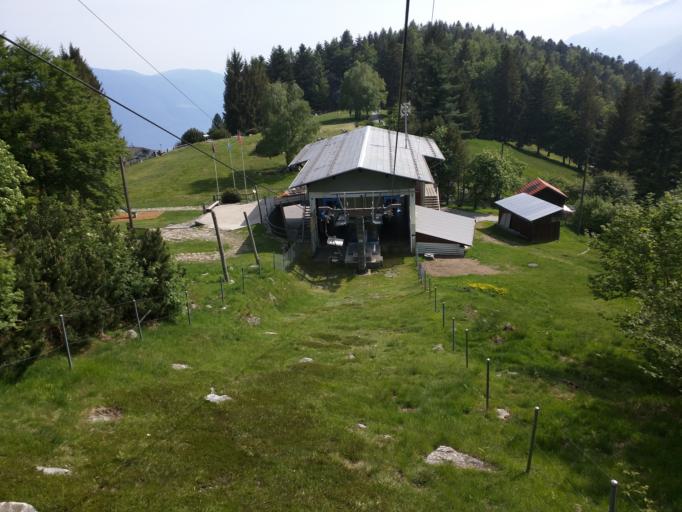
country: CH
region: Ticino
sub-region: Locarno District
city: Locarno
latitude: 46.1941
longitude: 8.7849
